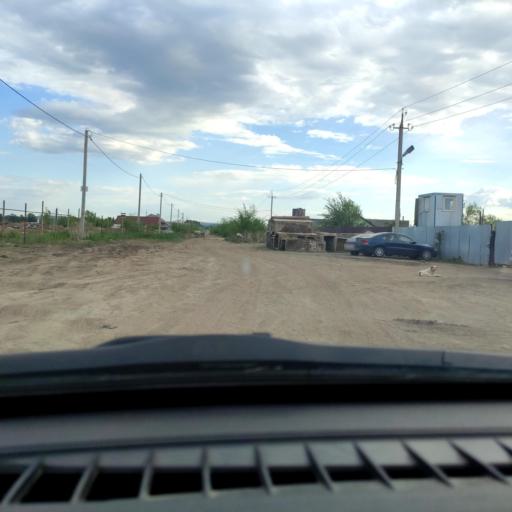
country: RU
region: Samara
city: Tol'yatti
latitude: 53.5765
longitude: 49.4145
